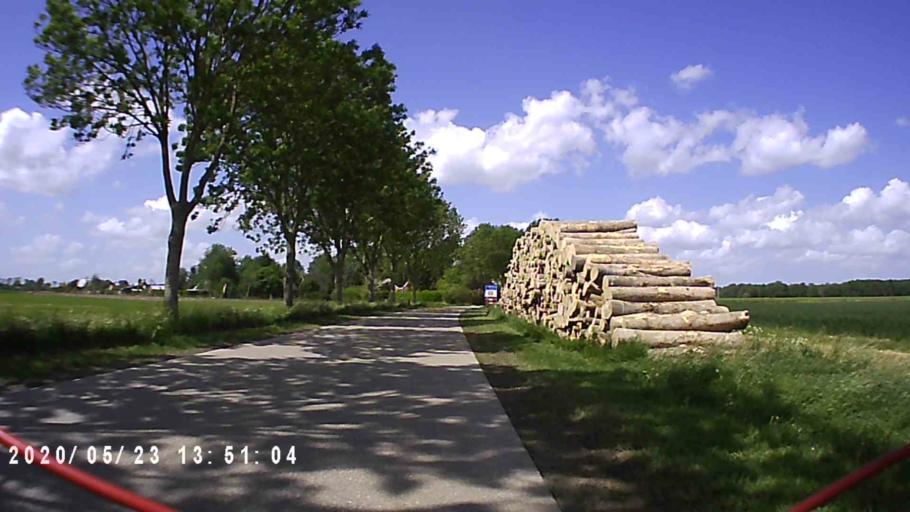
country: NL
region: Groningen
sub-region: Gemeente  Oldambt
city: Winschoten
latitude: 53.2672
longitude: 7.0391
